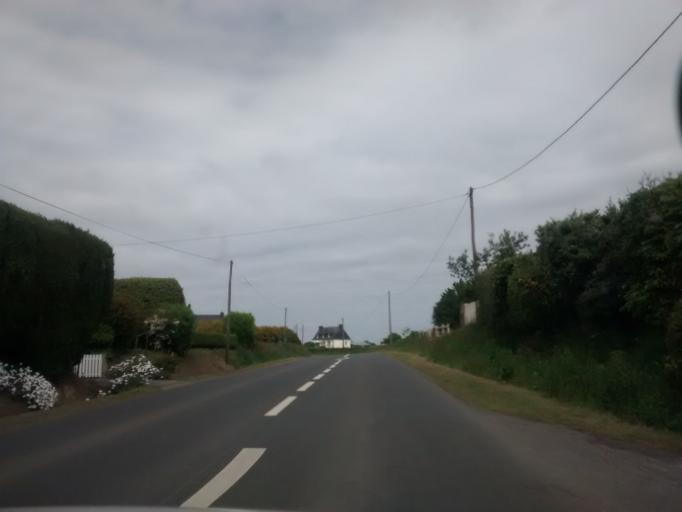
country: FR
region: Brittany
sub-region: Departement des Cotes-d'Armor
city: Penvenan
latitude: 48.7803
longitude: -3.3161
